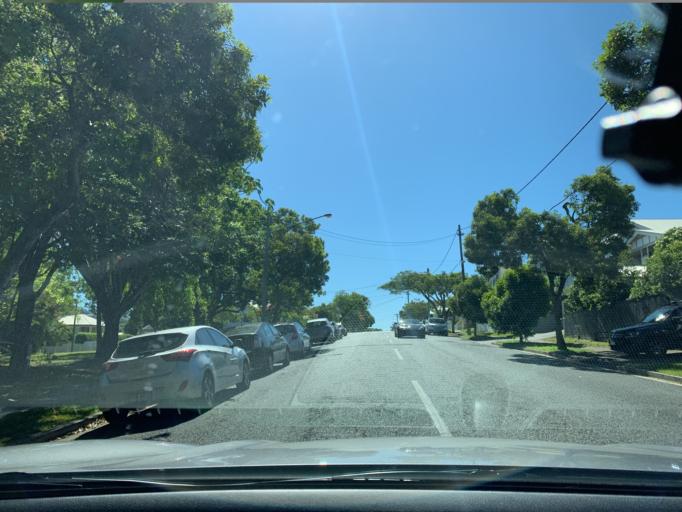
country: AU
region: Queensland
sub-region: Brisbane
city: Ascot
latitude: -27.4285
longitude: 153.0582
